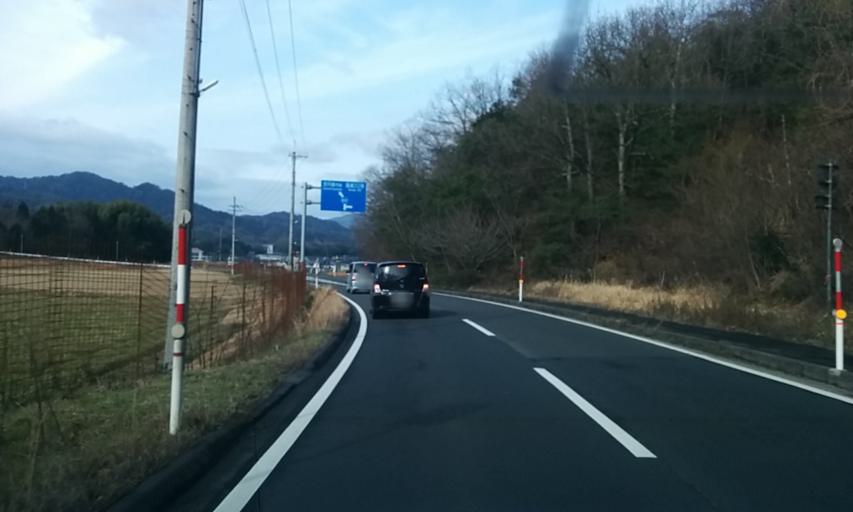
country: JP
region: Kyoto
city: Miyazu
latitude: 35.5836
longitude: 135.1076
